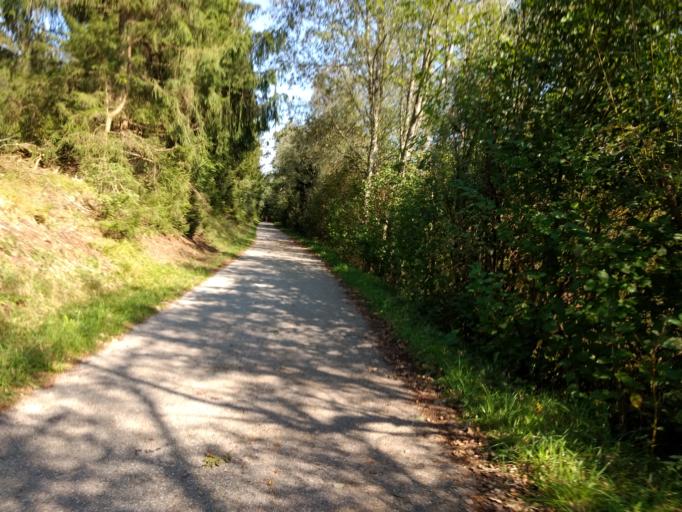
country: DE
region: Bavaria
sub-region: Upper Bavaria
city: Geretsried
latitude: 47.8400
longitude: 11.4770
